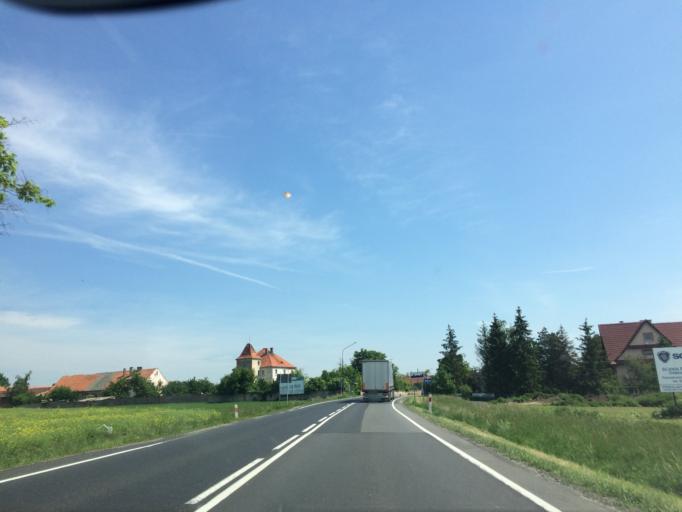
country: PL
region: Lower Silesian Voivodeship
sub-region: Powiat wroclawski
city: Gniechowice
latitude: 50.9632
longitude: 16.7923
